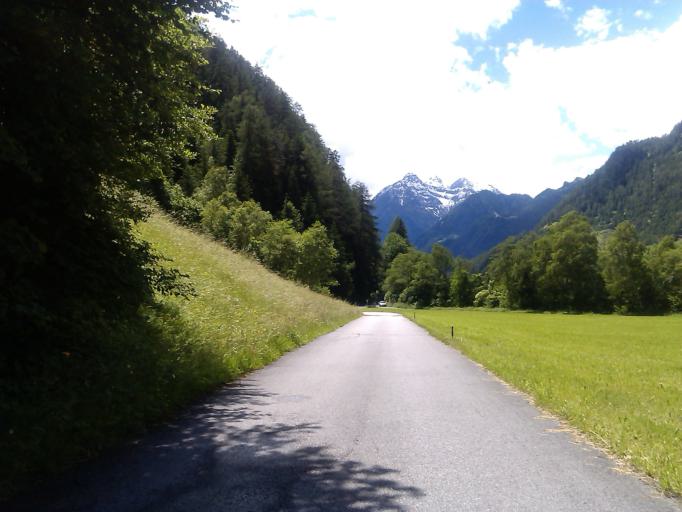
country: AT
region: Tyrol
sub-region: Politischer Bezirk Landeck
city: Pfunds
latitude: 46.9791
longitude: 10.5610
